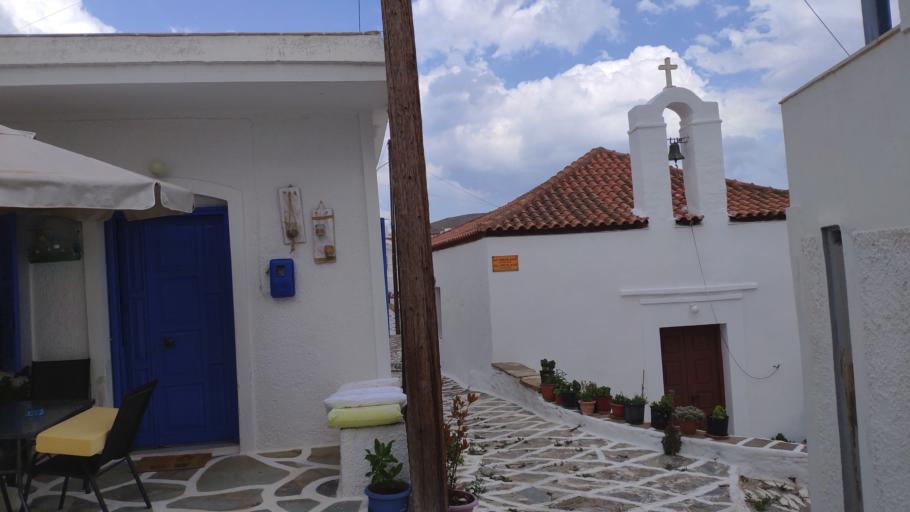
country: GR
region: South Aegean
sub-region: Nomos Kykladon
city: Kythnos
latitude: 37.4123
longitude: 24.4295
